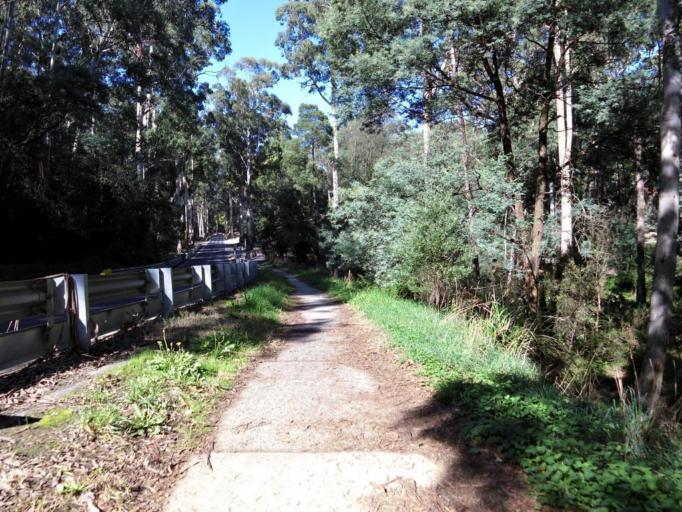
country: AU
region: Victoria
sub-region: Cardinia
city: Cockatoo
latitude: -37.9413
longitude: 145.4929
